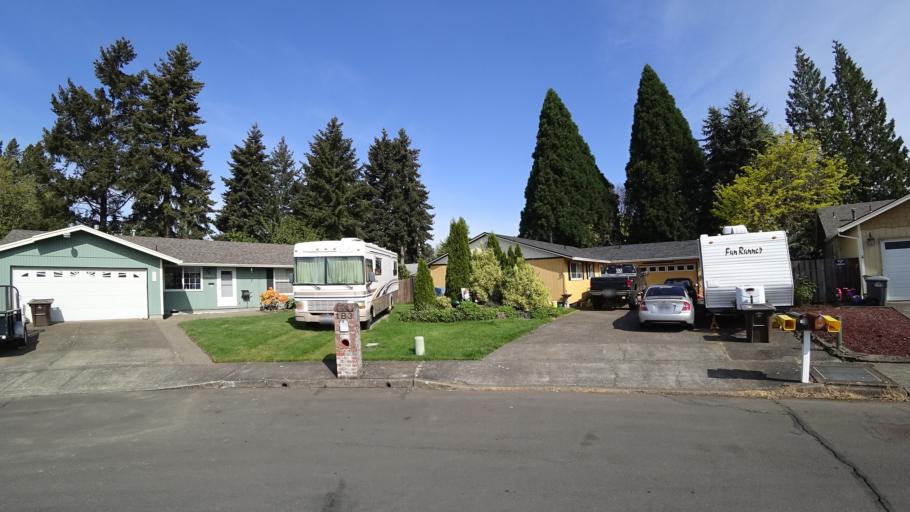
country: US
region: Oregon
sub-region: Washington County
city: Hillsboro
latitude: 45.5219
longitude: -122.9475
